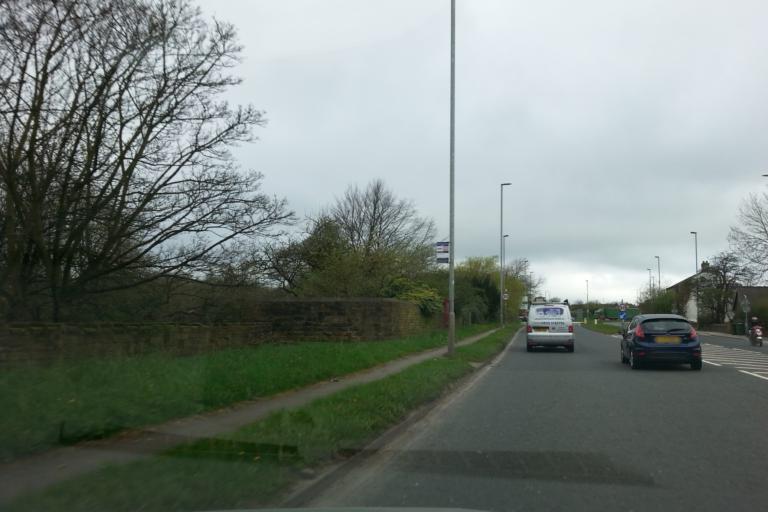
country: GB
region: England
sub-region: City and Borough of Leeds
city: Gildersome
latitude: 53.7486
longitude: -1.6310
